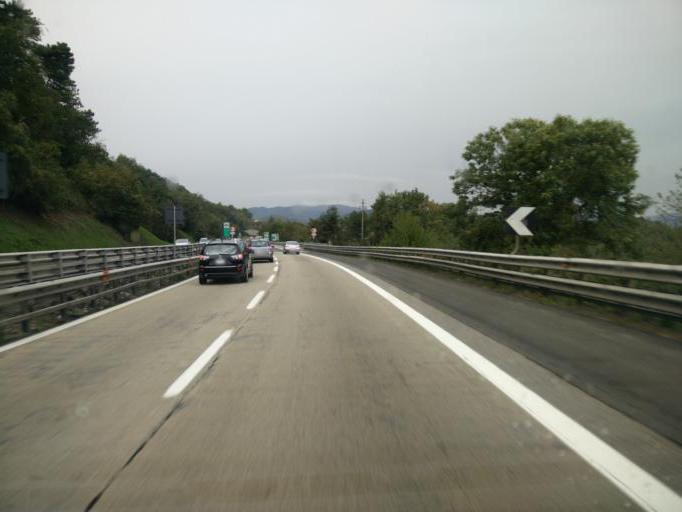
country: IT
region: Tuscany
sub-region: Province of Florence
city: Barberino di Mugello
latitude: 44.0193
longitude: 11.2244
